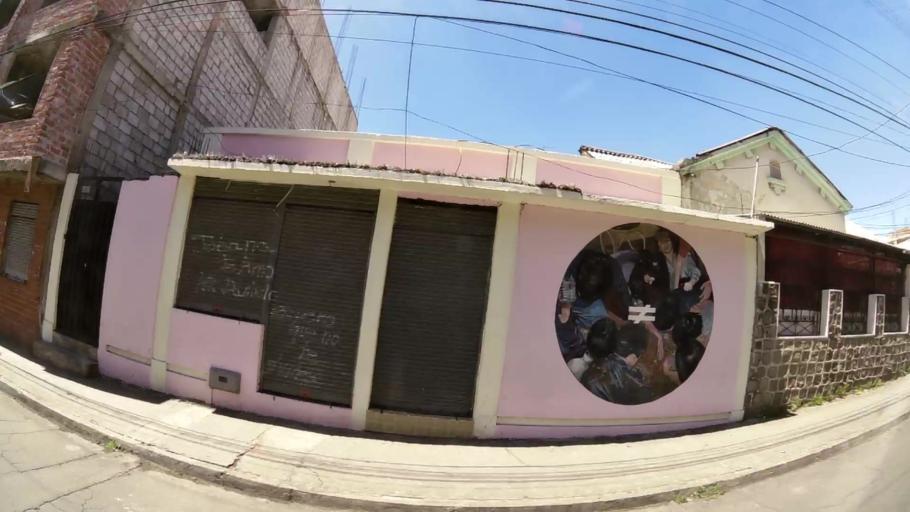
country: EC
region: Chimborazo
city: Riobamba
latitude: -1.6702
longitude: -78.6564
